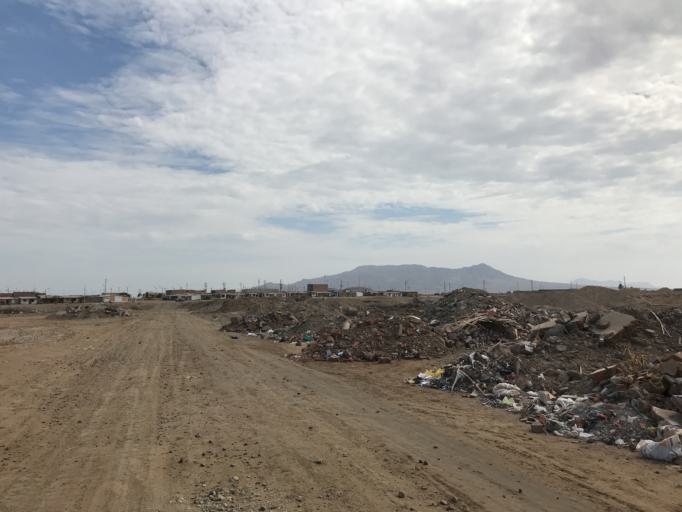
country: PE
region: Lambayeque
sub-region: Provincia de Chiclayo
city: Eten
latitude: -6.9010
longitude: -79.8442
